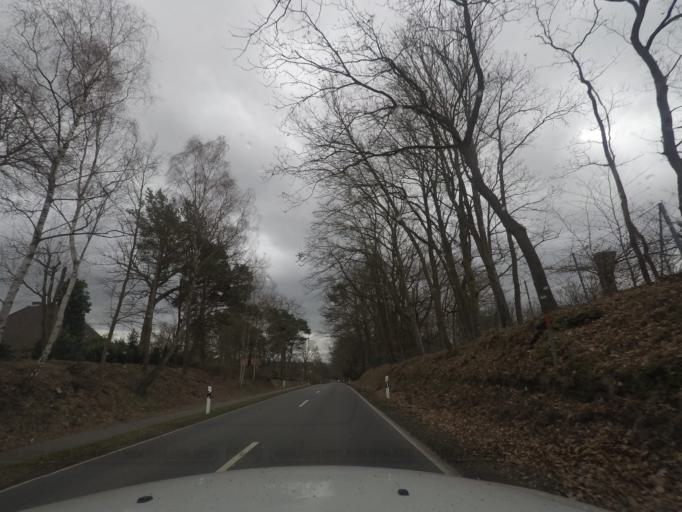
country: DE
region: Lower Saxony
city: Bad Bevensen
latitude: 53.0751
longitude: 10.5933
